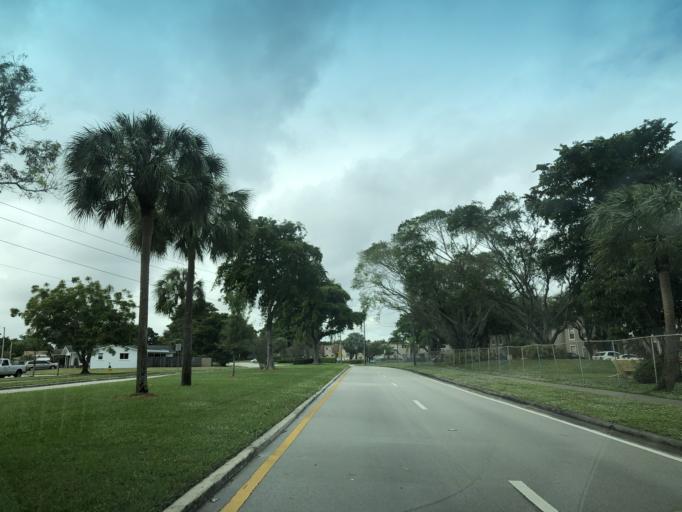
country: US
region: Florida
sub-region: Broward County
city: North Lauderdale
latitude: 26.2416
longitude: -80.2315
